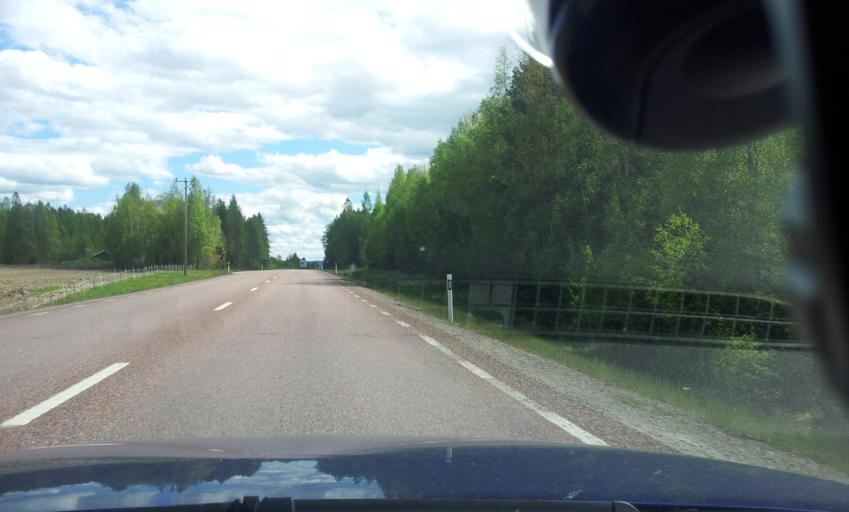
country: SE
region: Gaevleborg
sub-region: Ljusdals Kommun
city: Ljusdal
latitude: 61.7833
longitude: 16.1371
